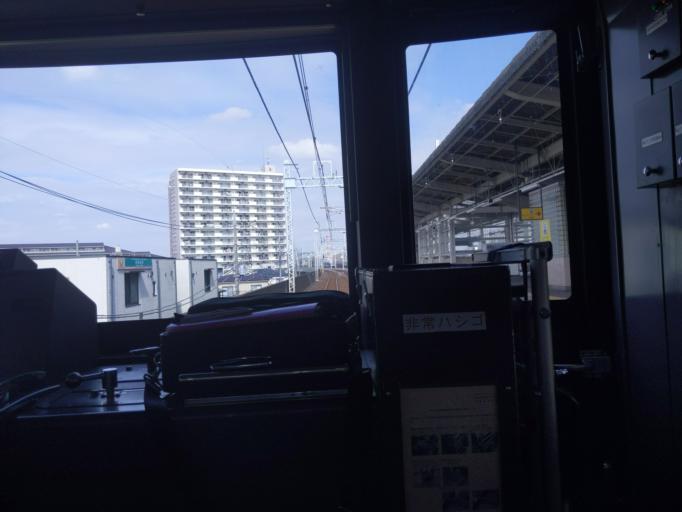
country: JP
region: Saitama
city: Soka
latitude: 35.8144
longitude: 139.8011
